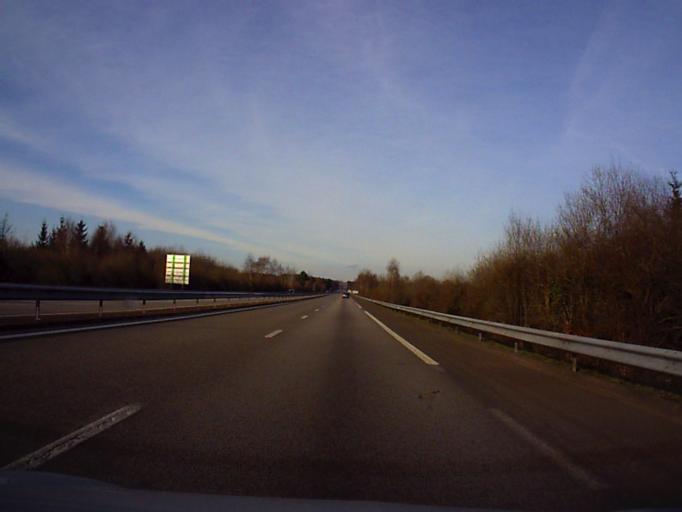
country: FR
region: Brittany
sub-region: Departement du Morbihan
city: Malestroit
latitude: 47.8339
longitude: -2.4294
